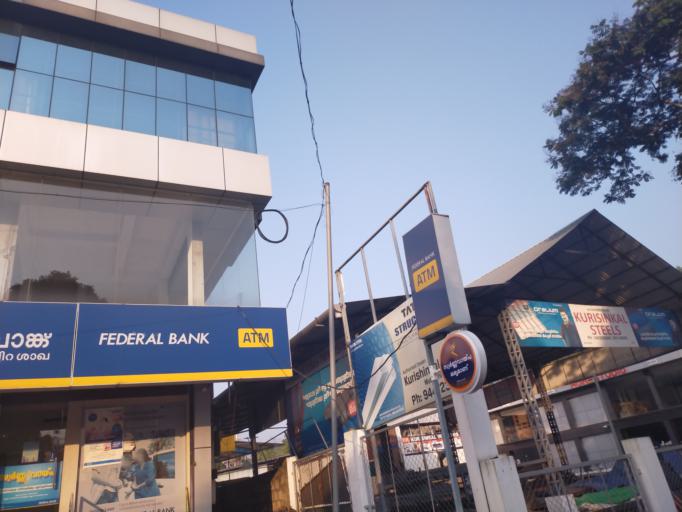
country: IN
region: Kerala
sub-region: Kottayam
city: Vaikam
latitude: 9.7551
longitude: 76.5004
